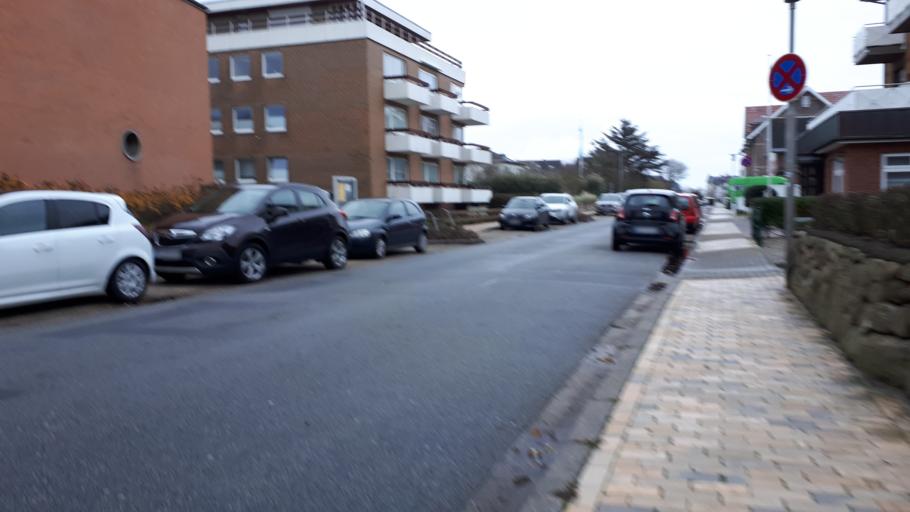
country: DE
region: Schleswig-Holstein
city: Westerland
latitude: 54.9054
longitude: 8.3014
